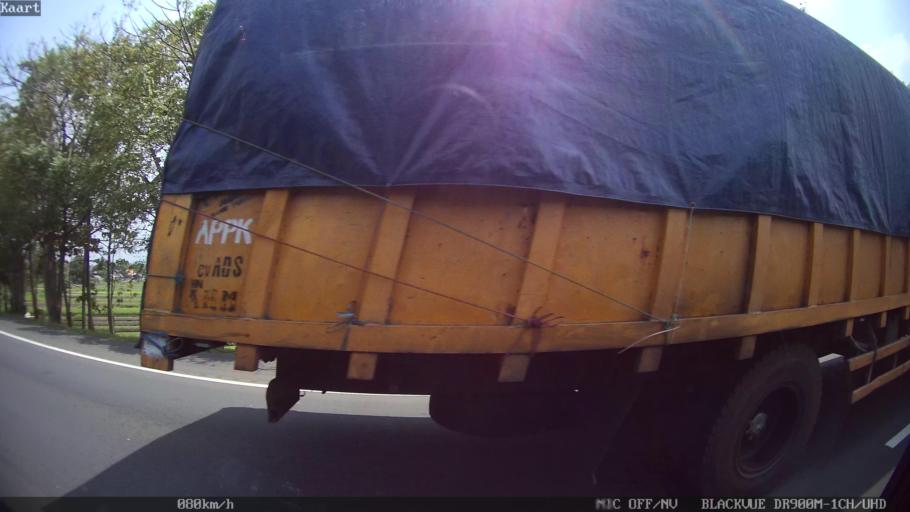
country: ID
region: Banten
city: Serang
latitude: -6.0502
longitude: 106.1159
